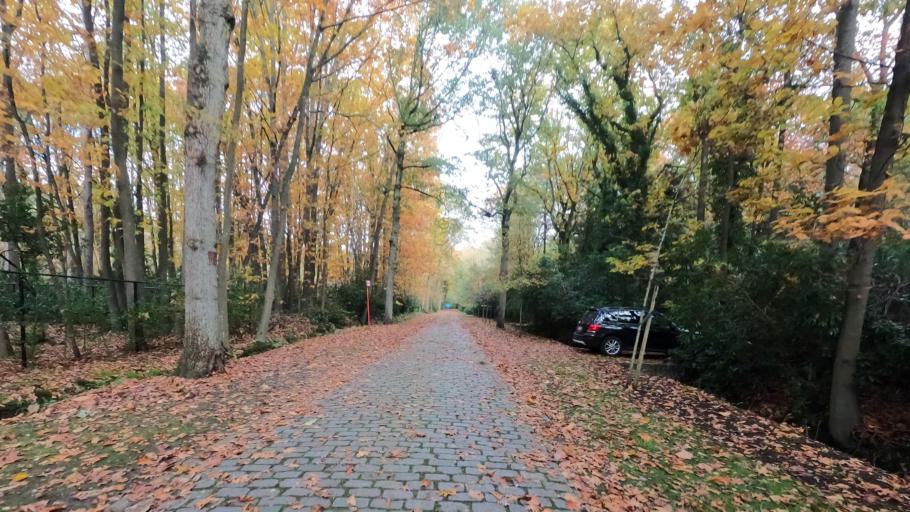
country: BE
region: Flanders
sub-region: Provincie Antwerpen
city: Brasschaat
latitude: 51.3431
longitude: 4.5232
